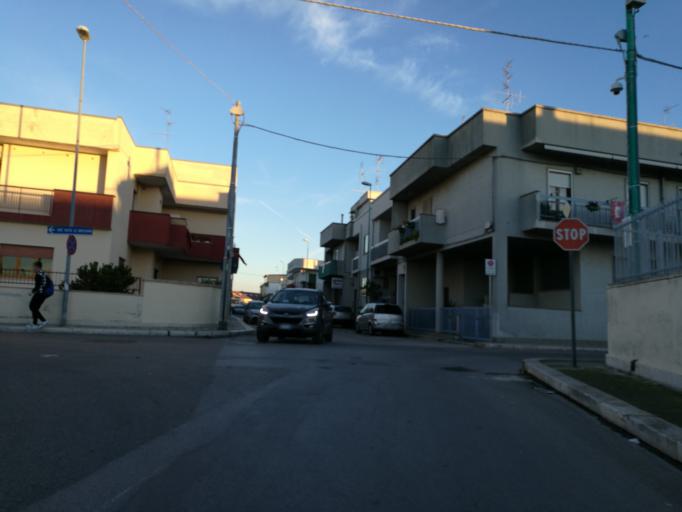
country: IT
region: Apulia
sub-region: Provincia di Bari
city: Adelfia
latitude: 41.0067
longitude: 16.8776
